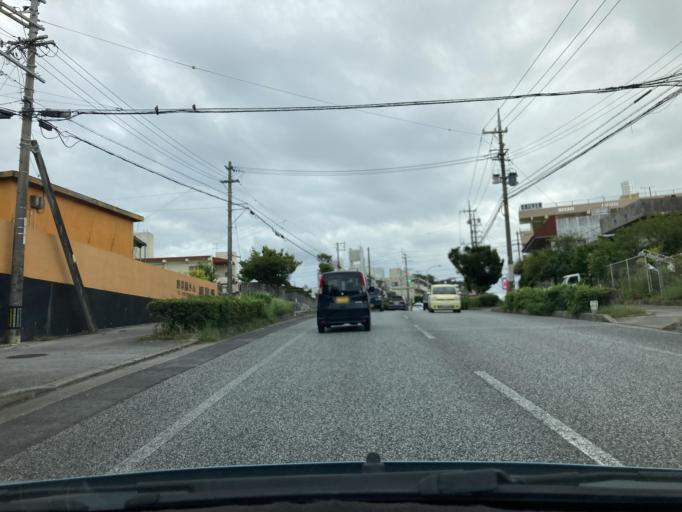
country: JP
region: Okinawa
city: Ginowan
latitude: 26.2516
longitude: 127.7576
